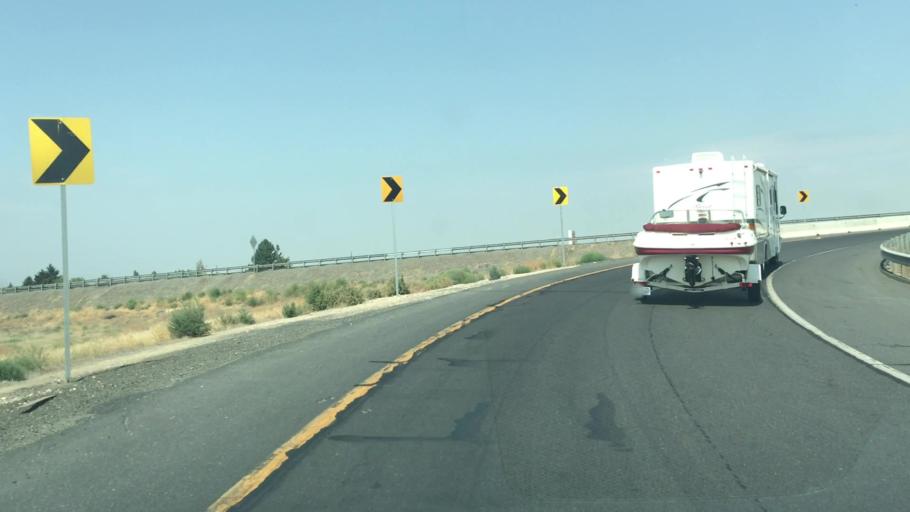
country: US
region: Washington
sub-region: Grant County
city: Quincy
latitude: 47.1014
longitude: -119.8310
